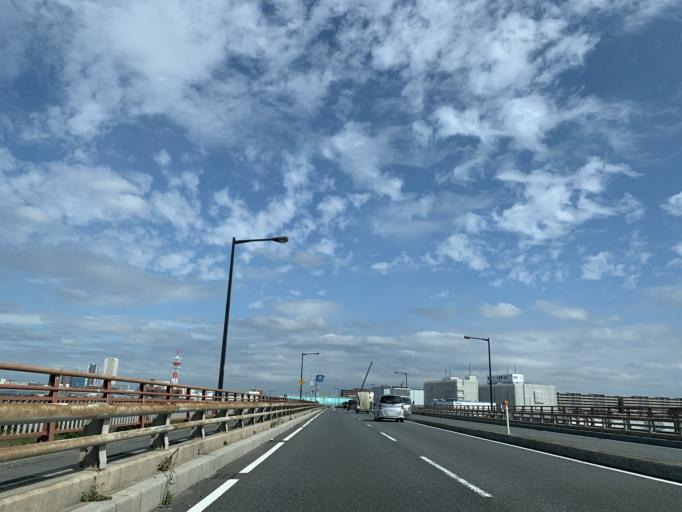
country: JP
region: Tokyo
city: Urayasu
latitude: 35.7026
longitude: 139.9258
